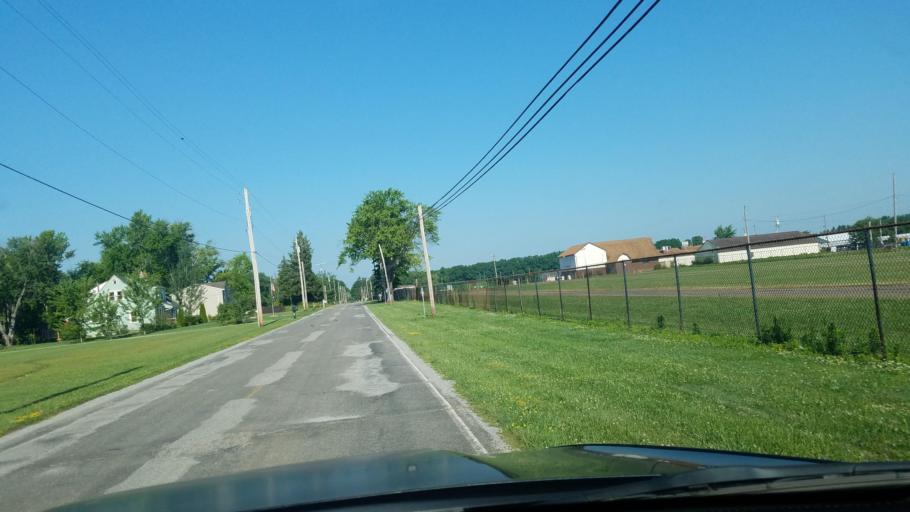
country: US
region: Ohio
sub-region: Trumbull County
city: Cortland
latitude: 41.3301
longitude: -80.7869
